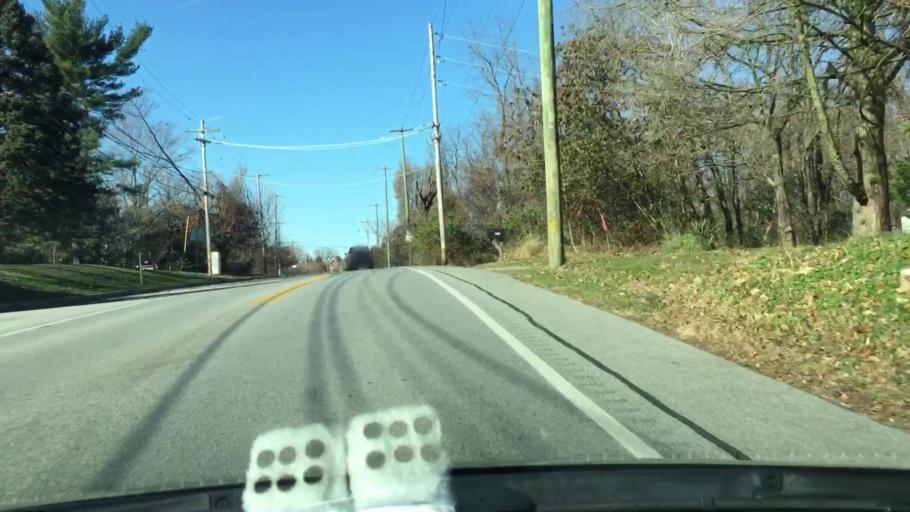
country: US
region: Pennsylvania
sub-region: Delaware County
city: Chester Heights
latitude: 39.8482
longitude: -75.5342
